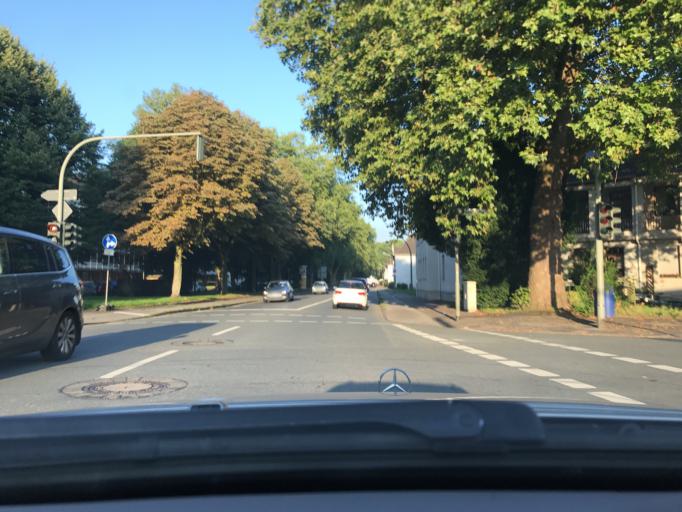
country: DE
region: North Rhine-Westphalia
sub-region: Regierungsbezirk Dusseldorf
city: Hochfeld
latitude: 51.4067
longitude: 6.7200
